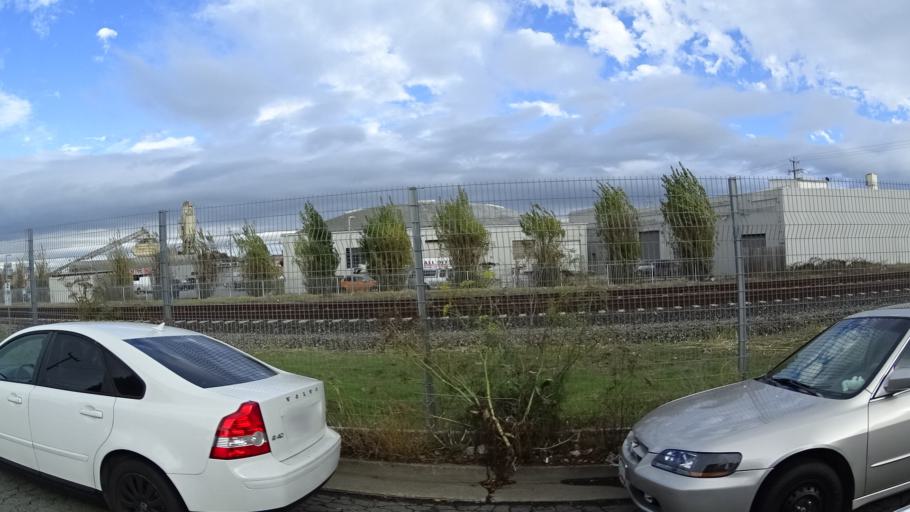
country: US
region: California
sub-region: San Mateo County
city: San Bruno
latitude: 37.6412
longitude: -122.4134
